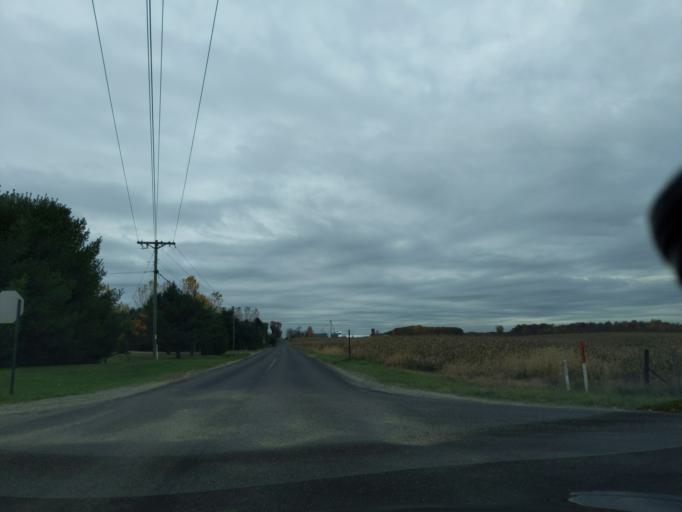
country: US
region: Michigan
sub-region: Eaton County
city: Eaton Rapids
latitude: 42.4657
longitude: -84.6008
